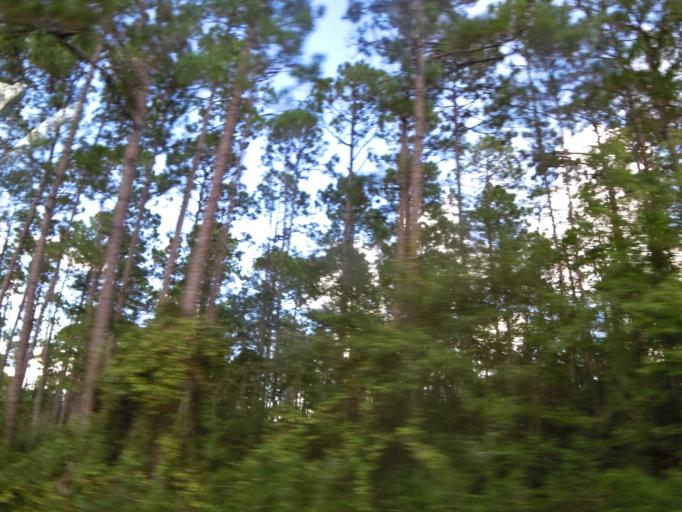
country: US
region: Georgia
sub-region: Echols County
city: Statenville
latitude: 30.7461
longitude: -83.1043
